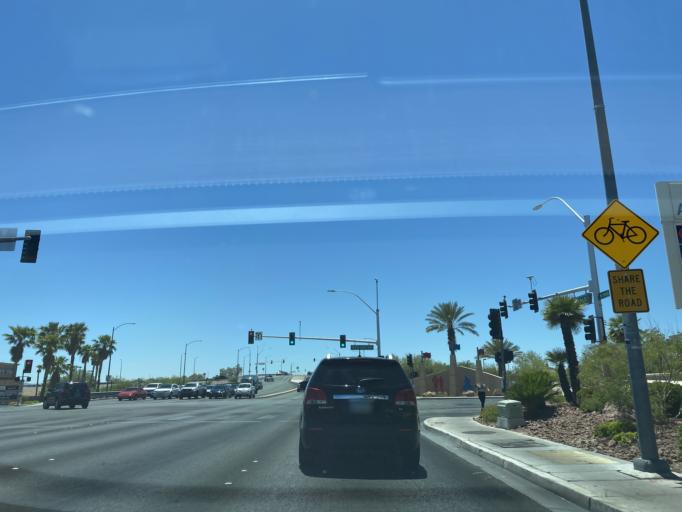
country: US
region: Nevada
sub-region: Clark County
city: Spring Valley
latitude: 36.1817
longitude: -115.2601
